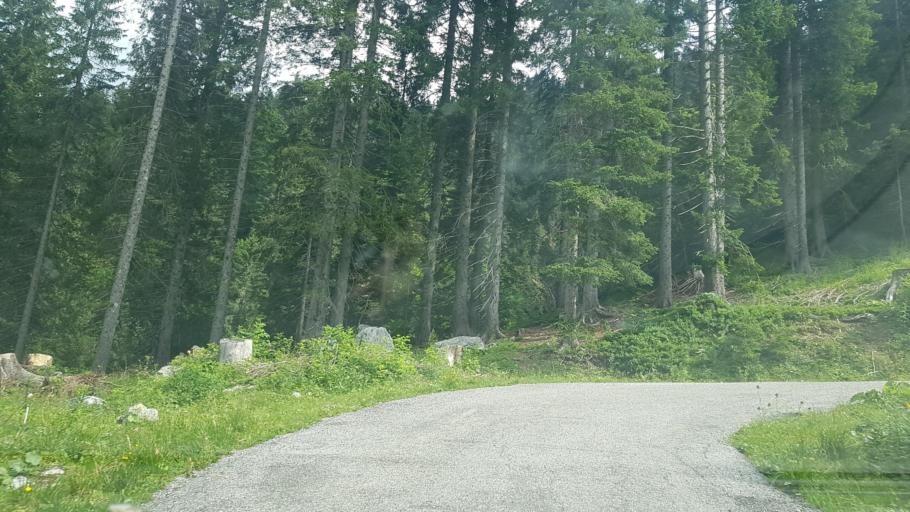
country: IT
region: Friuli Venezia Giulia
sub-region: Provincia di Udine
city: Paularo
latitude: 46.5735
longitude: 13.1603
